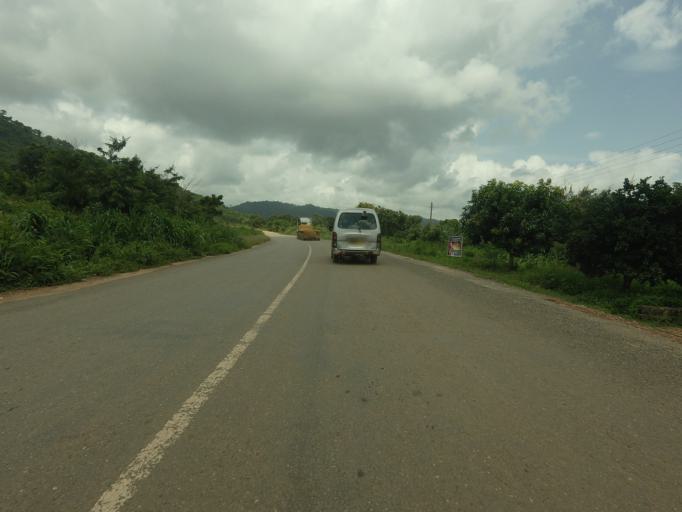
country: GH
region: Volta
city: Ho
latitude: 6.7051
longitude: 0.3341
